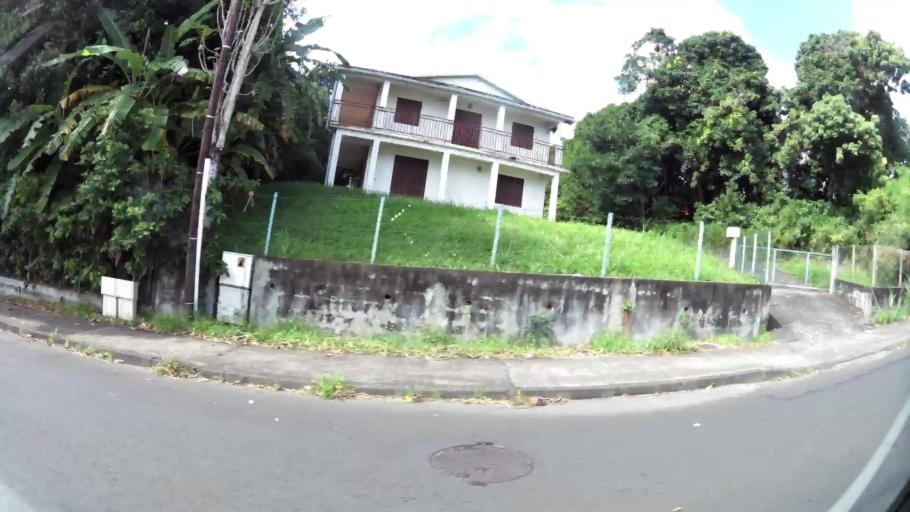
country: RE
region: Reunion
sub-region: Reunion
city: Saint-Denis
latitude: -20.9305
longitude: 55.4931
